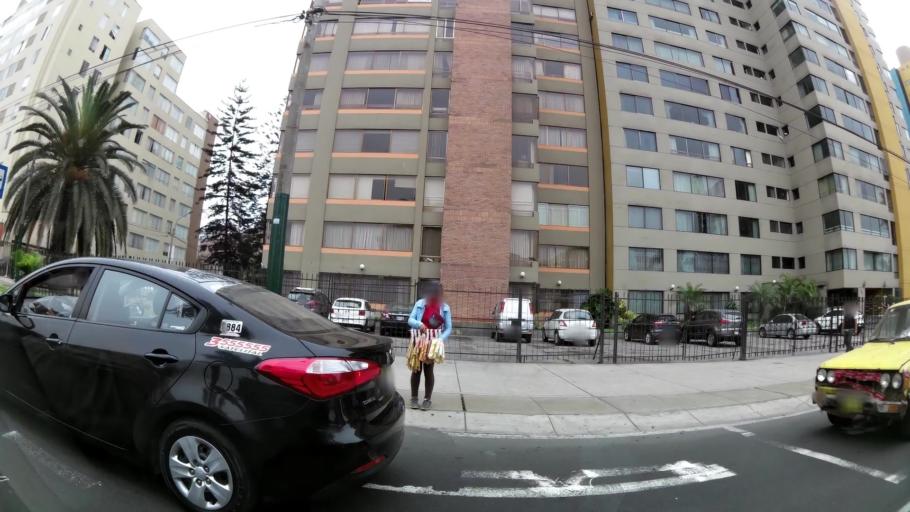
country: PE
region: Lima
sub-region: Lima
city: San Isidro
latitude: -12.0929
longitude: -77.0371
